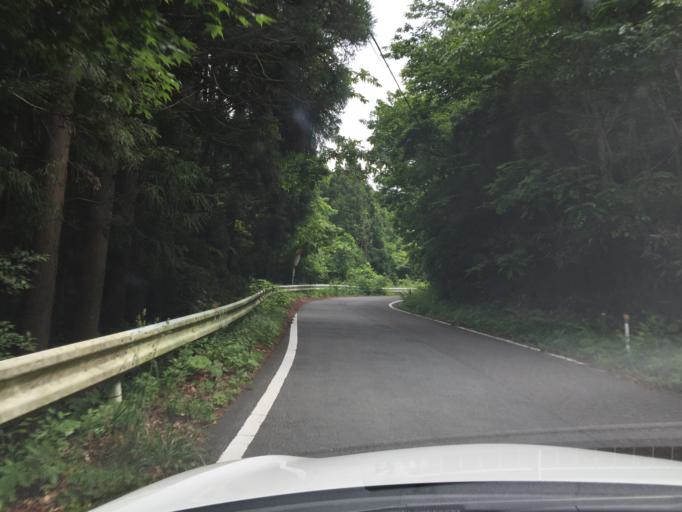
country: JP
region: Fukushima
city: Sukagawa
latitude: 37.2687
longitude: 140.5010
